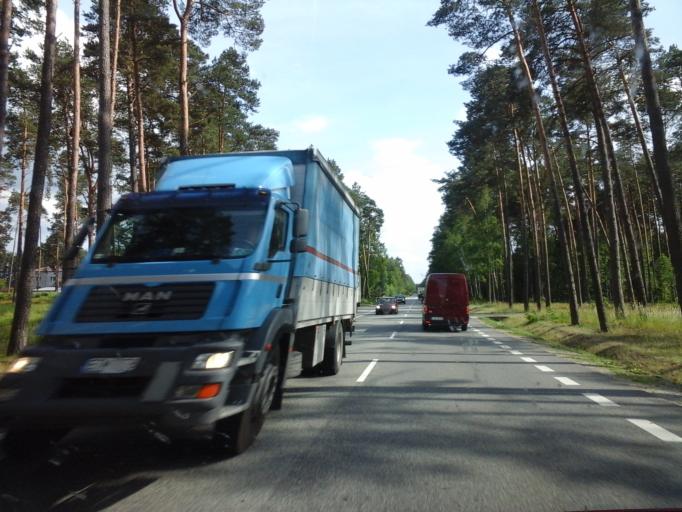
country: PL
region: Swietokrzyskie
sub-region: Powiat konecki
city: Ruda Maleniecka
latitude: 51.1783
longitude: 20.2202
